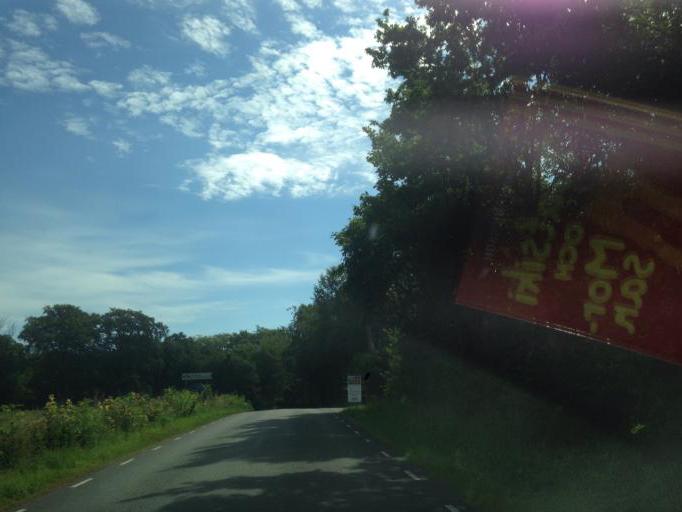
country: SE
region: Skane
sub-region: Tomelilla Kommun
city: Tomelilla
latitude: 55.6440
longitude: 14.0453
